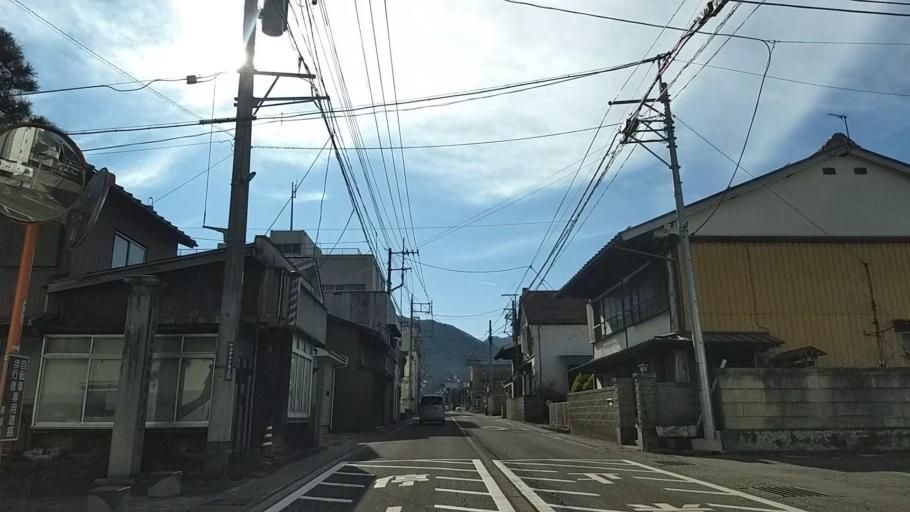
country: JP
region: Yamanashi
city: Otsuki
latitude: 35.5506
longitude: 138.9074
